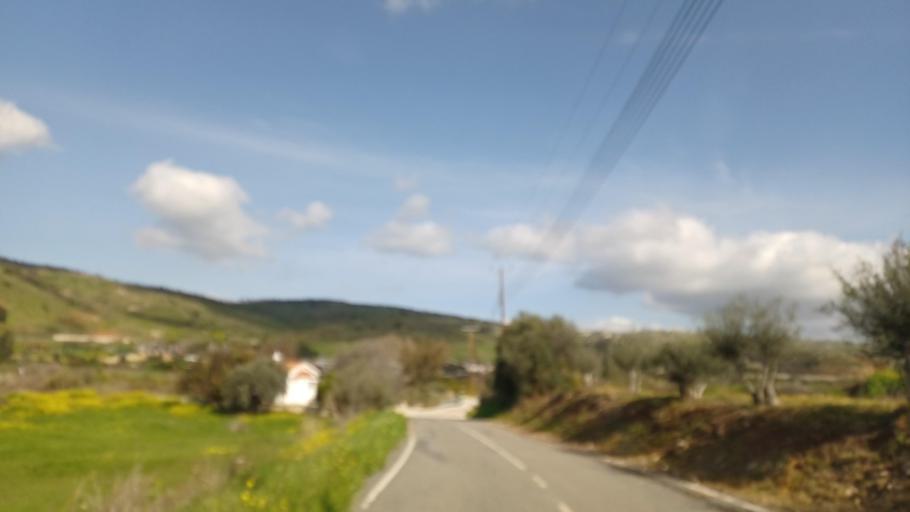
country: CY
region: Limassol
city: Pissouri
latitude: 34.7656
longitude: 32.6384
